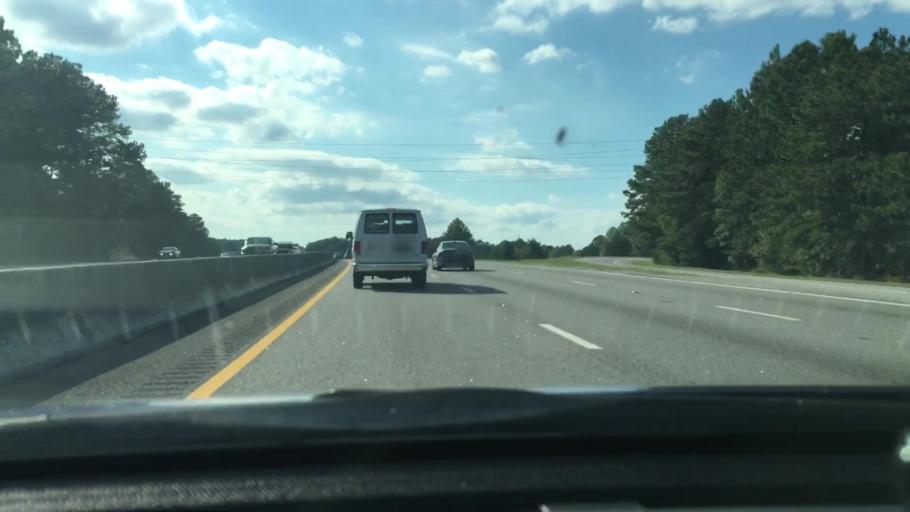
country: US
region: South Carolina
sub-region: Richland County
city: Dentsville
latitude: 34.0742
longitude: -80.9643
